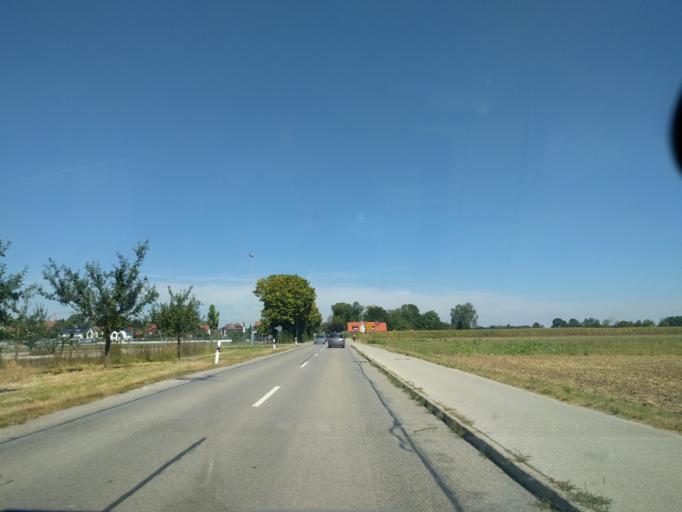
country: DE
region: Bavaria
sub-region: Upper Bavaria
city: Fuerstenfeldbruck
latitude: 48.1841
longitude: 11.2251
